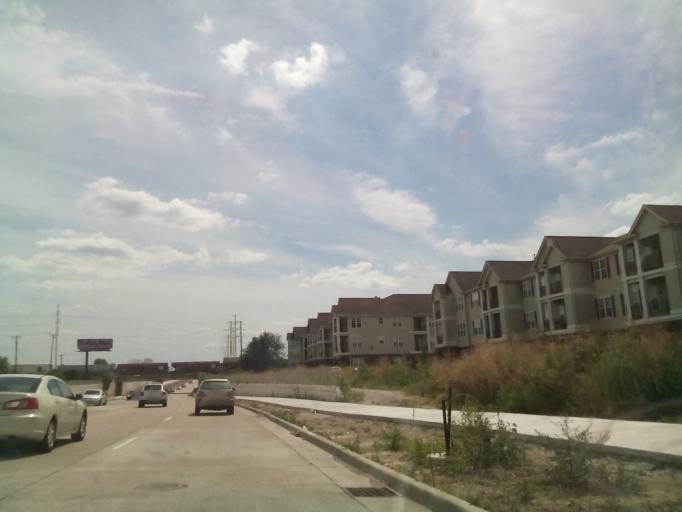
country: US
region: Illinois
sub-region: DuPage County
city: Warrenville
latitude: 41.7801
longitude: -88.2059
